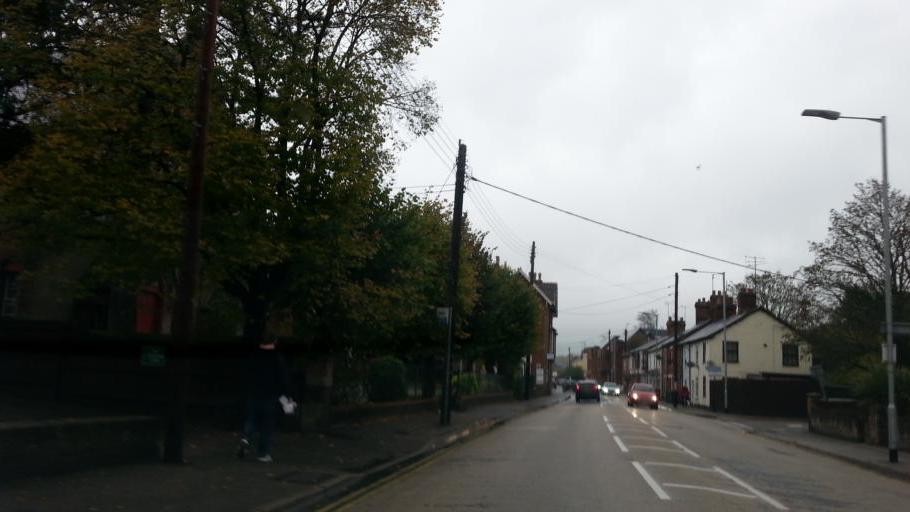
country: GB
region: England
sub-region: Suffolk
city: Haverhill
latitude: 52.0852
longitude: 0.4357
